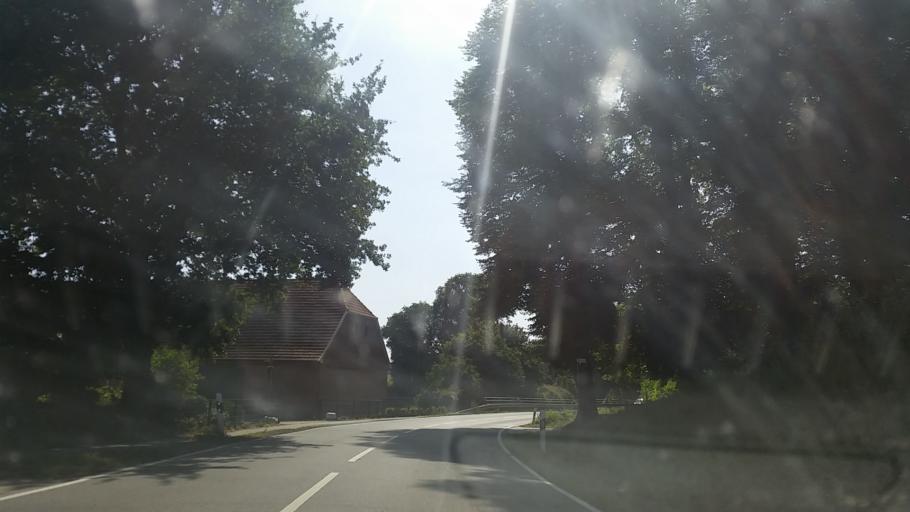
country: DE
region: Lower Saxony
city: Ankum
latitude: 52.5302
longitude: 7.8930
